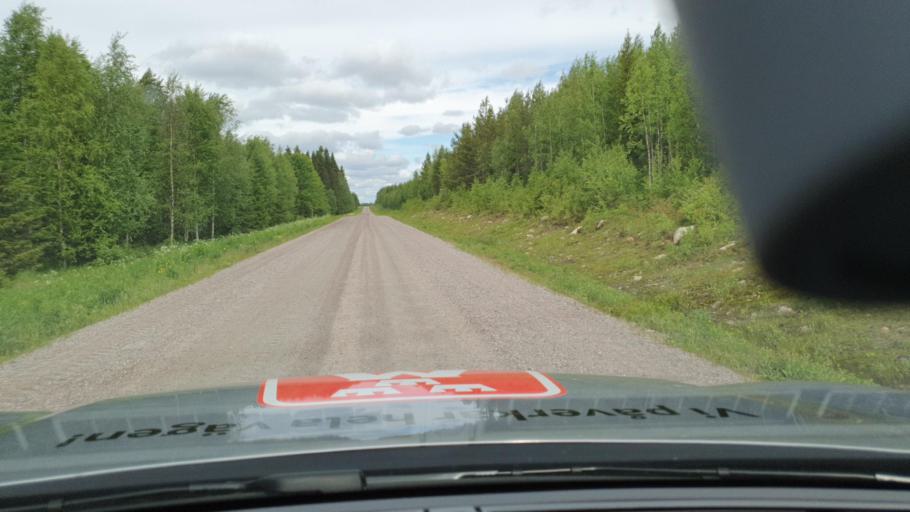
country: SE
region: Norrbotten
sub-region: Haparanda Kommun
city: Haparanda
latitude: 65.9575
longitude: 23.8040
